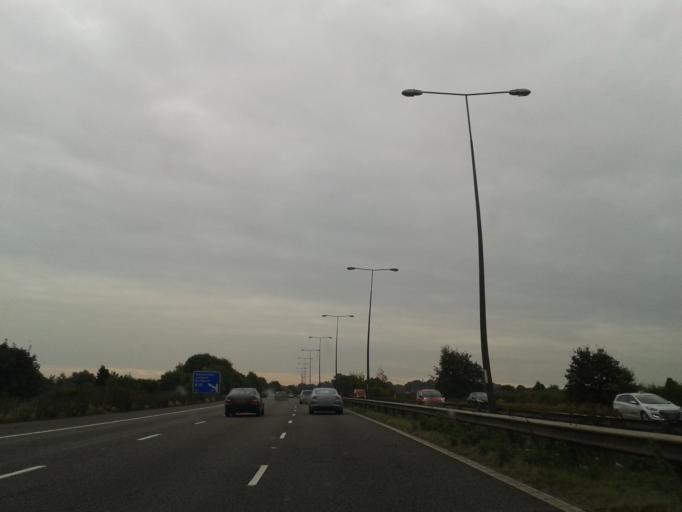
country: GB
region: England
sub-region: Borough of Wigan
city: Shevington
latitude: 53.5512
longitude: -2.7011
